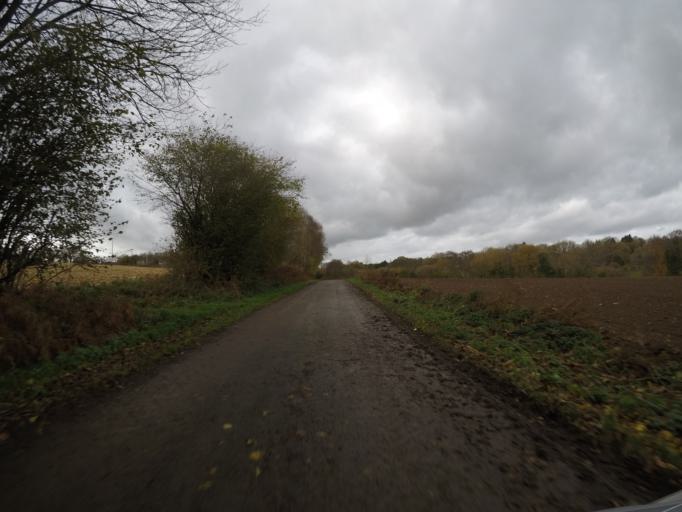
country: FR
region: Brittany
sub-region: Departement des Cotes-d'Armor
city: Bourbriac
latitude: 48.4671
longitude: -3.2223
